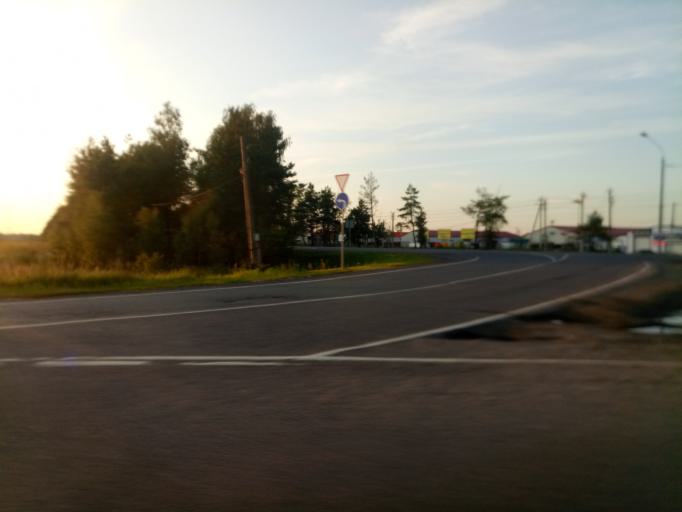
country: RU
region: Moskovskaya
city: Noginsk-9
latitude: 56.1123
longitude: 38.6152
